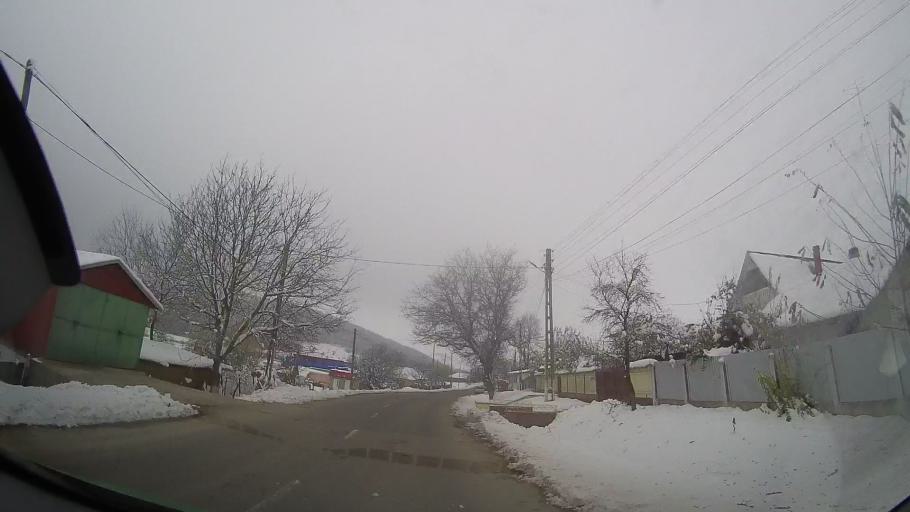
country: RO
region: Neamt
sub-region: Comuna Oniceni
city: Oniceni
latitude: 46.7999
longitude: 27.1475
